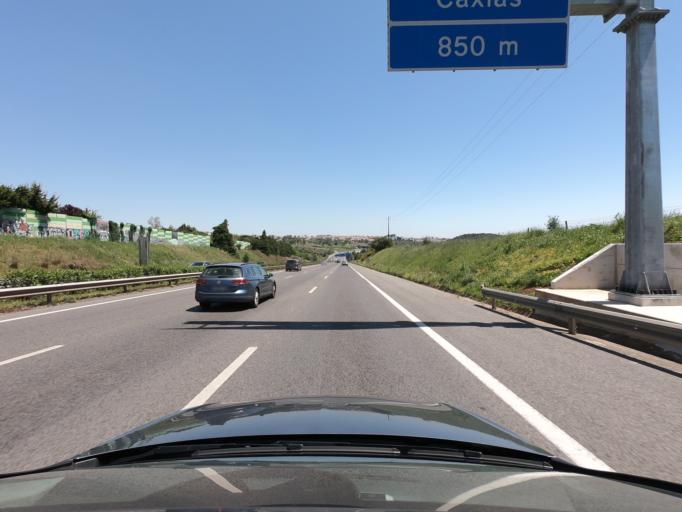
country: PT
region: Lisbon
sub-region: Oeiras
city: Terrugem
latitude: 38.7144
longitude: -9.2811
